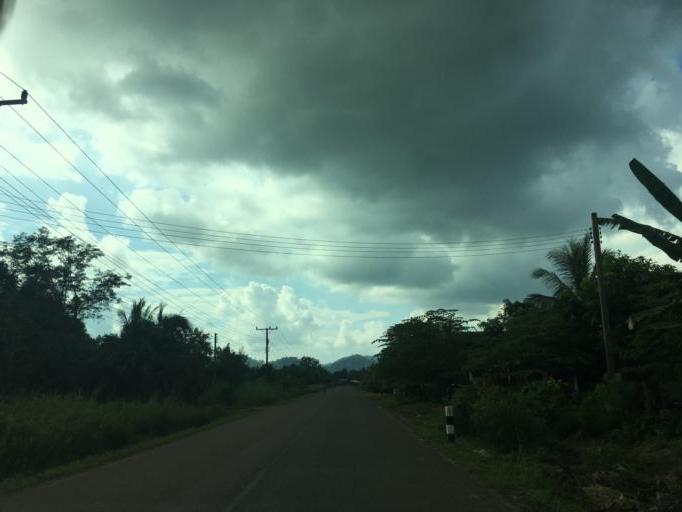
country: TH
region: Nong Khai
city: Sangkhom
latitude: 18.1525
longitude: 102.2668
